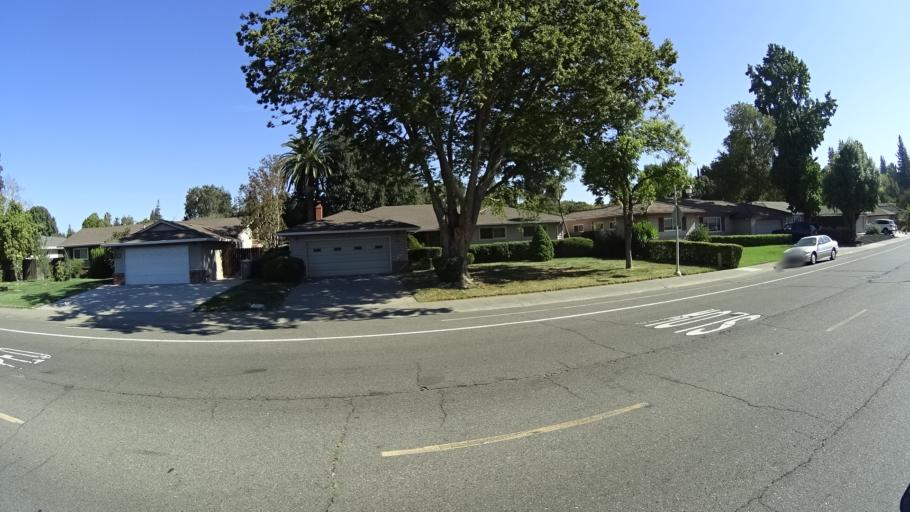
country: US
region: California
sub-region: Sacramento County
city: Parkway
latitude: 38.5111
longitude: -121.5246
